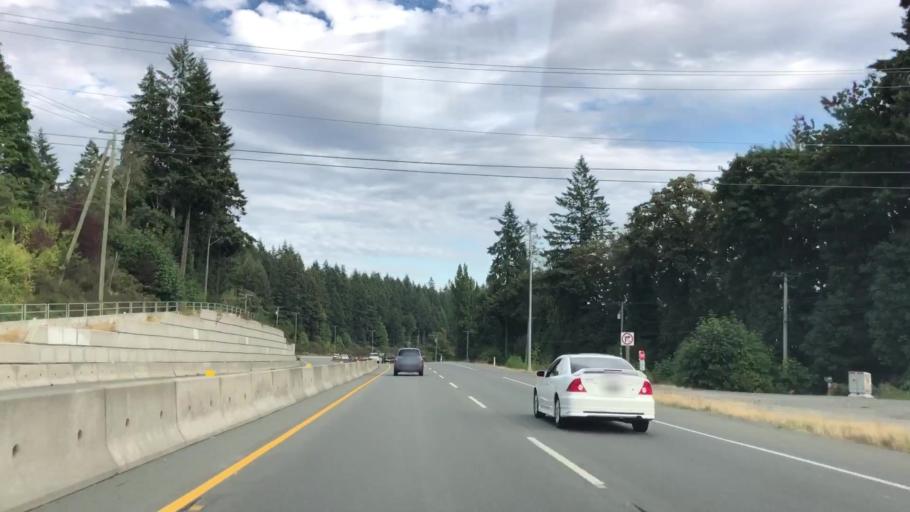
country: CA
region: British Columbia
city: Duncan
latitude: 48.7188
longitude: -123.6208
